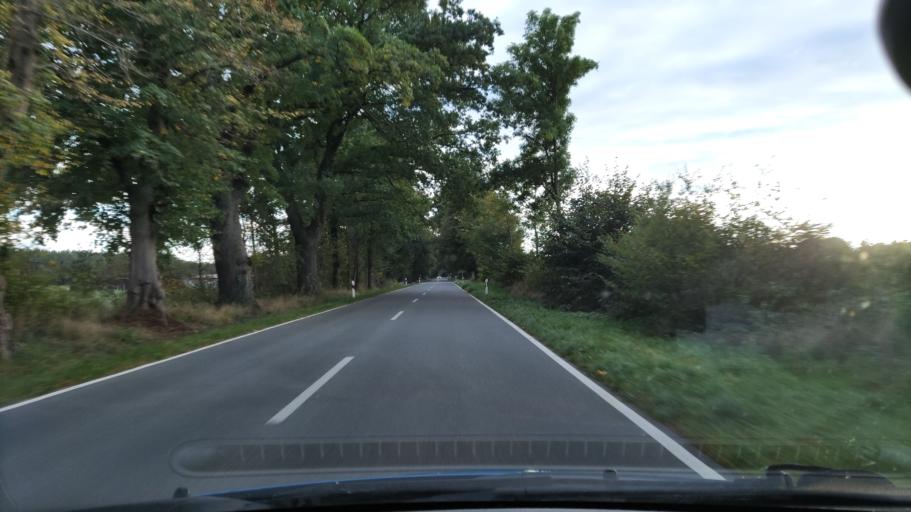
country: DE
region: Mecklenburg-Vorpommern
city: Boizenburg
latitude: 53.4050
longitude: 10.8267
